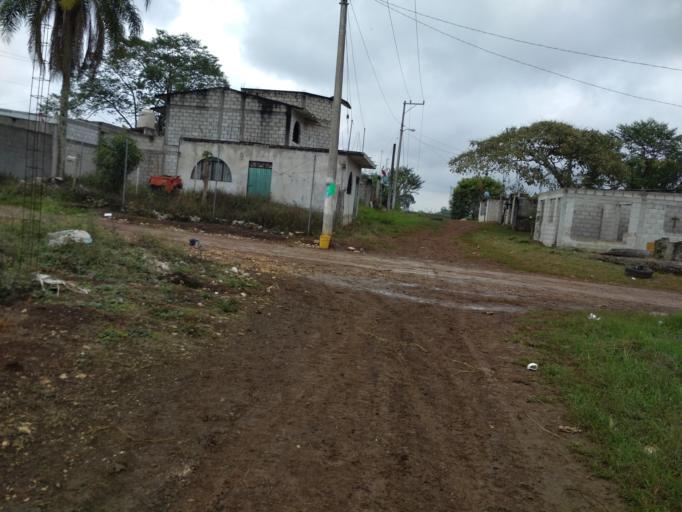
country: MX
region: Veracruz
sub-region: Cordoba
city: San Jose de Tapia
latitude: 18.8510
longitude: -96.9677
